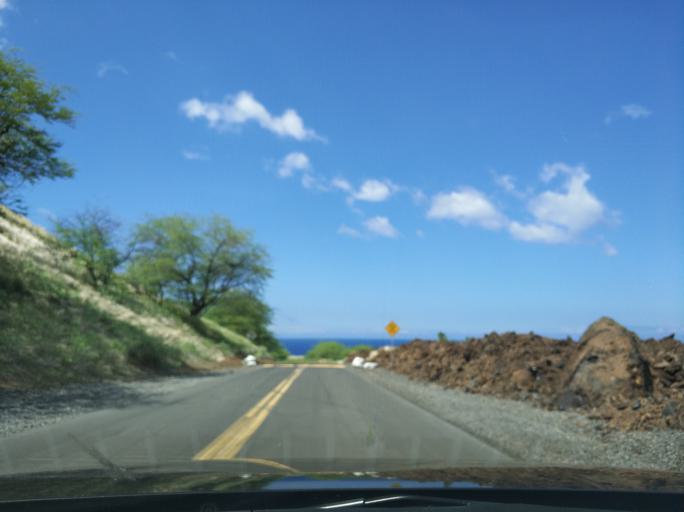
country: US
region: Hawaii
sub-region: Hawaii County
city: Kalaoa
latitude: 19.8004
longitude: -156.0082
